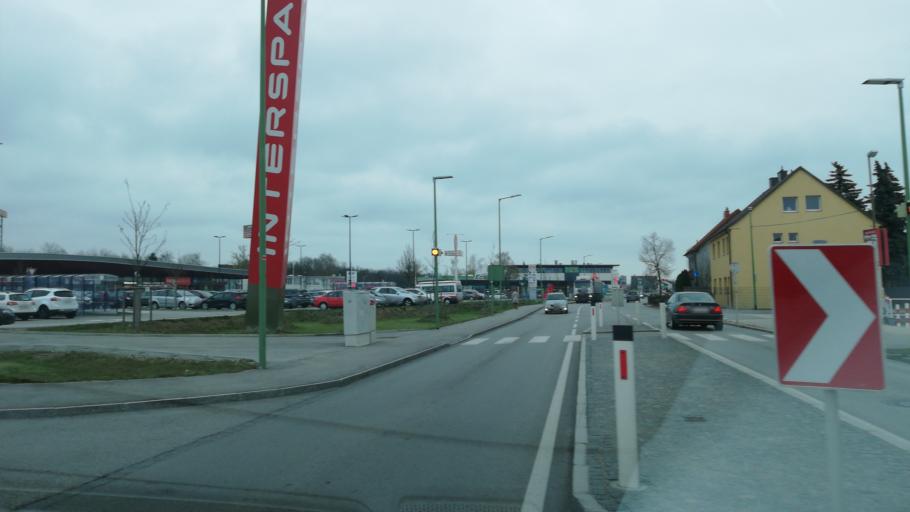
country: AT
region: Upper Austria
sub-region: Wels Stadt
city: Wels
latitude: 48.1815
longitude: 14.0138
